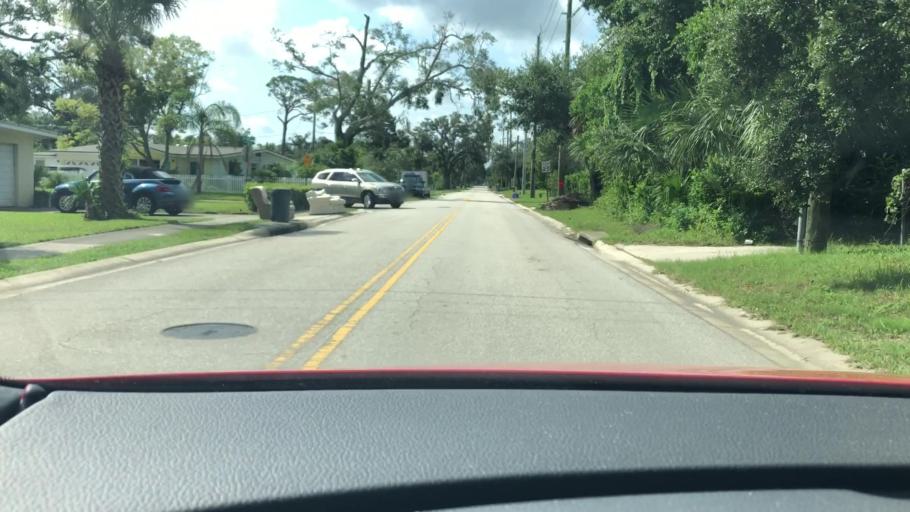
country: US
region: Florida
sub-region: Volusia County
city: Ormond Beach
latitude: 29.2741
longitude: -81.0537
